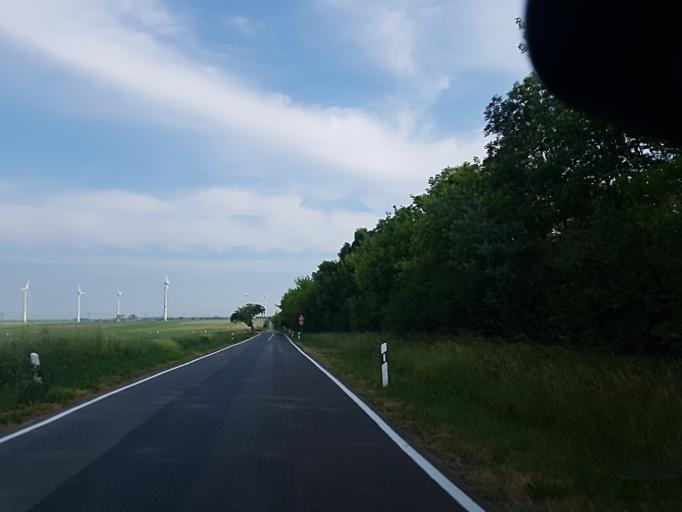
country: DE
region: Saxony-Anhalt
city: Zahna
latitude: 51.9786
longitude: 12.8248
